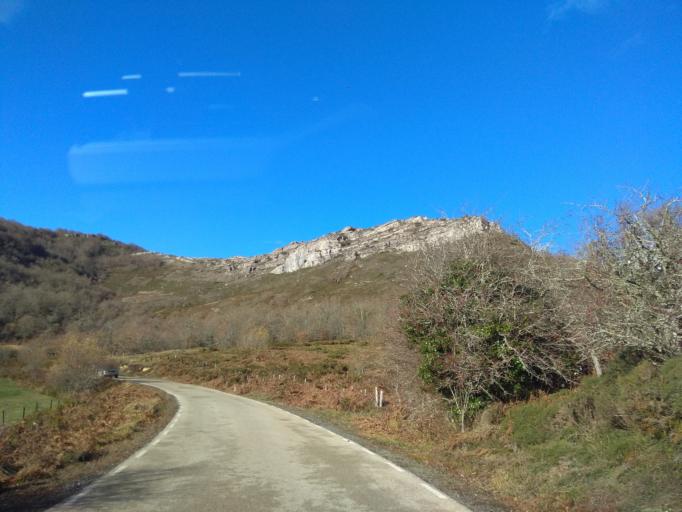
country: ES
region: Cantabria
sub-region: Provincia de Cantabria
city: San Martin de Elines
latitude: 42.9352
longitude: -3.8316
